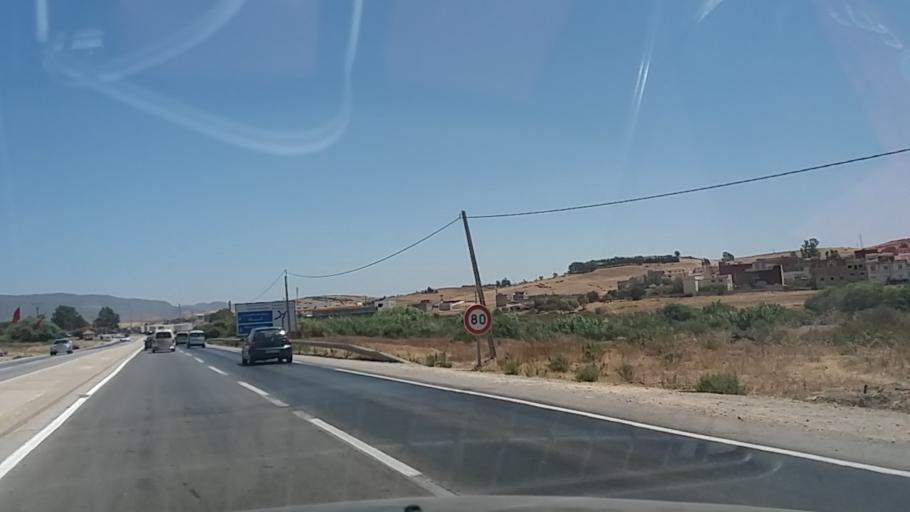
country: MA
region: Tanger-Tetouan
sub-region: Tanger-Assilah
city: Tangier
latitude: 35.6790
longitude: -5.7093
